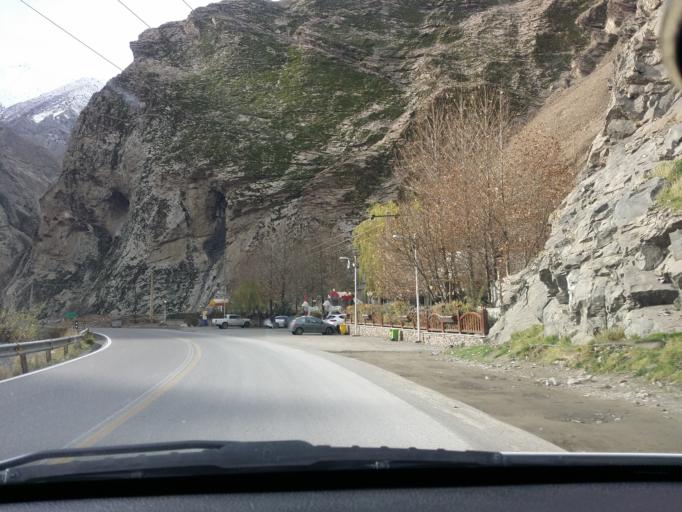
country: IR
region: Tehran
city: Tajrish
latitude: 36.0314
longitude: 51.2292
